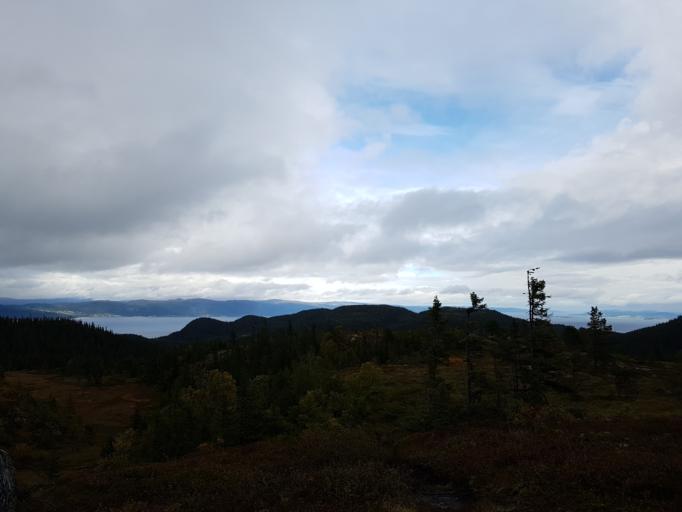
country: NO
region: Sor-Trondelag
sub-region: Melhus
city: Melhus
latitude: 63.4150
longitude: 10.2197
